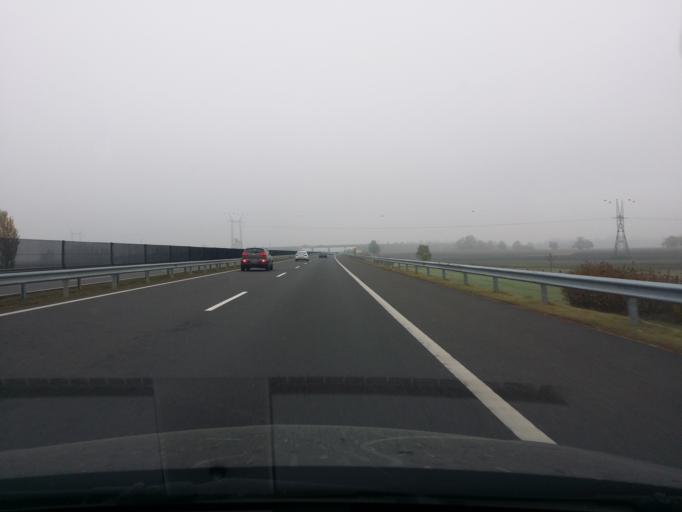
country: HU
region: Hajdu-Bihar
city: Hajdunanas
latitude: 47.8585
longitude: 21.3588
